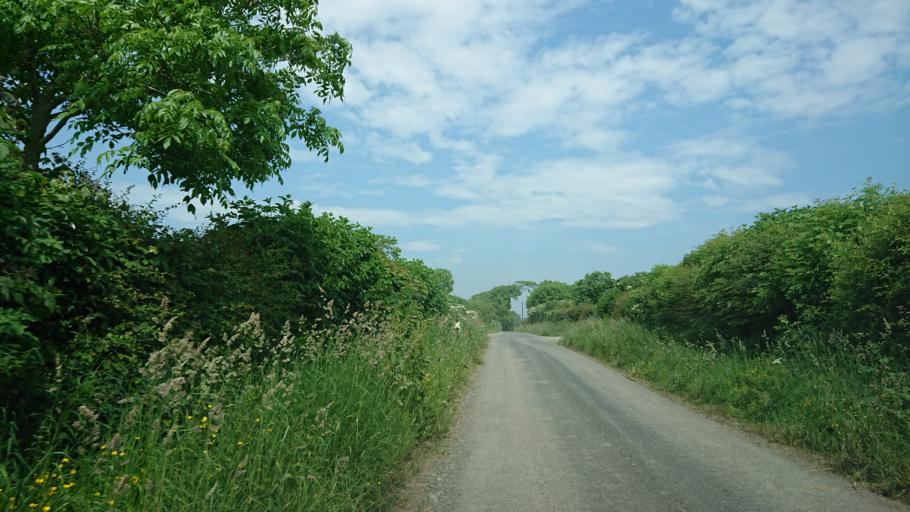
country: IE
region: Munster
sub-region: Waterford
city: Dunmore East
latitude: 52.2187
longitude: -7.0008
